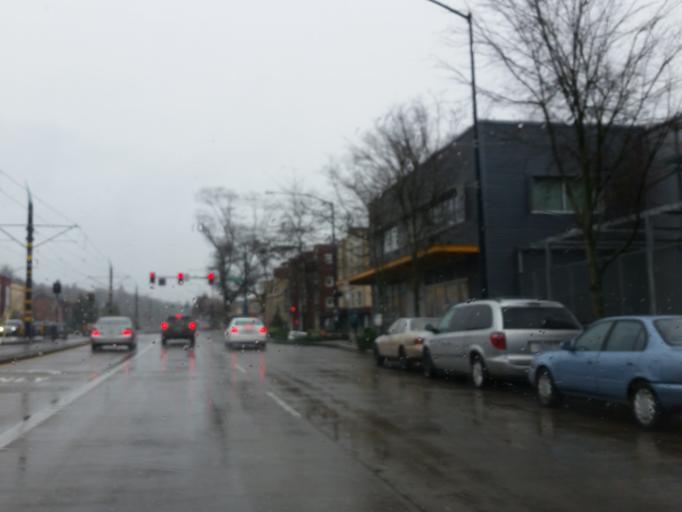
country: US
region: Washington
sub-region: King County
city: Seattle
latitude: 47.5631
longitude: -122.2949
